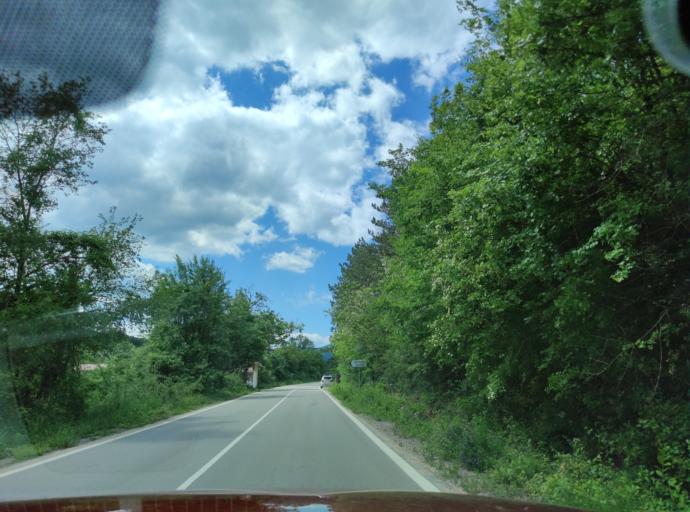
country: BG
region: Montana
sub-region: Obshtina Chiprovtsi
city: Chiprovtsi
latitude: 43.4523
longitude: 22.9069
